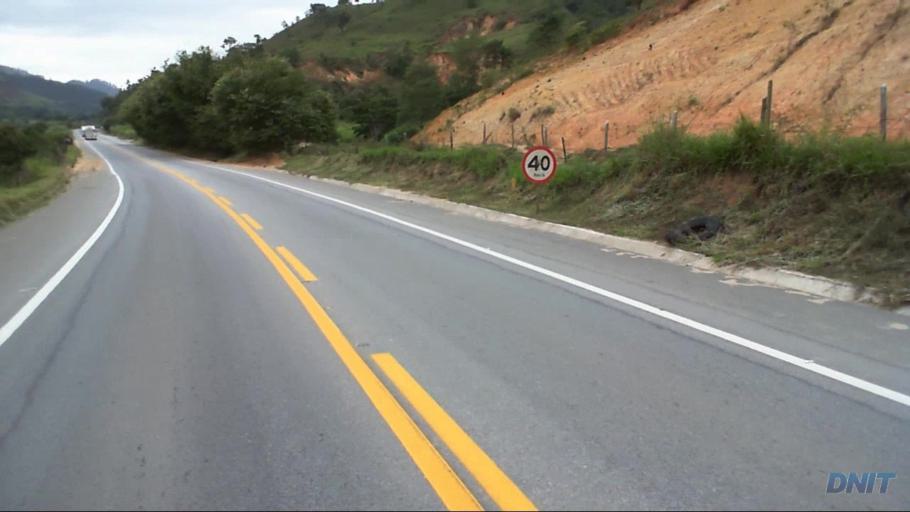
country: BR
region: Minas Gerais
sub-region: Timoteo
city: Timoteo
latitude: -19.6127
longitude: -42.7688
